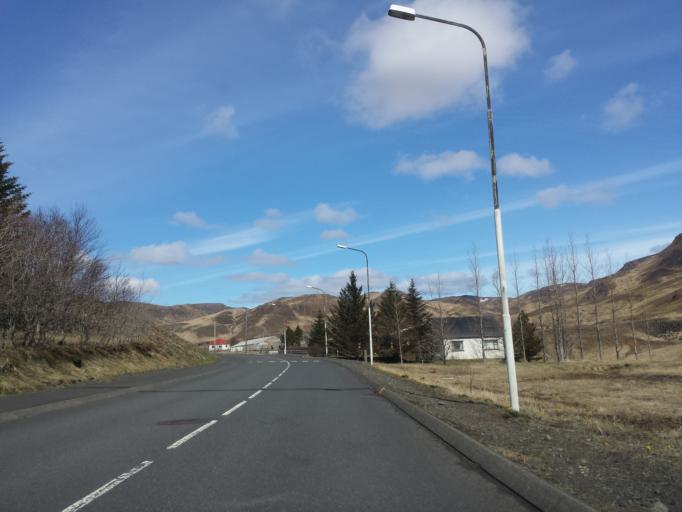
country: IS
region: South
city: Hveragerdi
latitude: 64.0072
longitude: -21.1877
